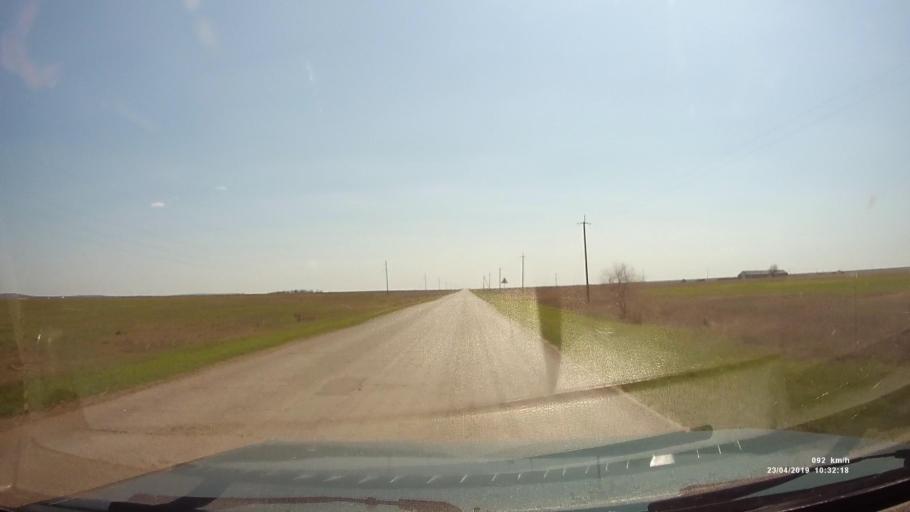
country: RU
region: Kalmykiya
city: Yashalta
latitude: 46.5811
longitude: 42.5756
